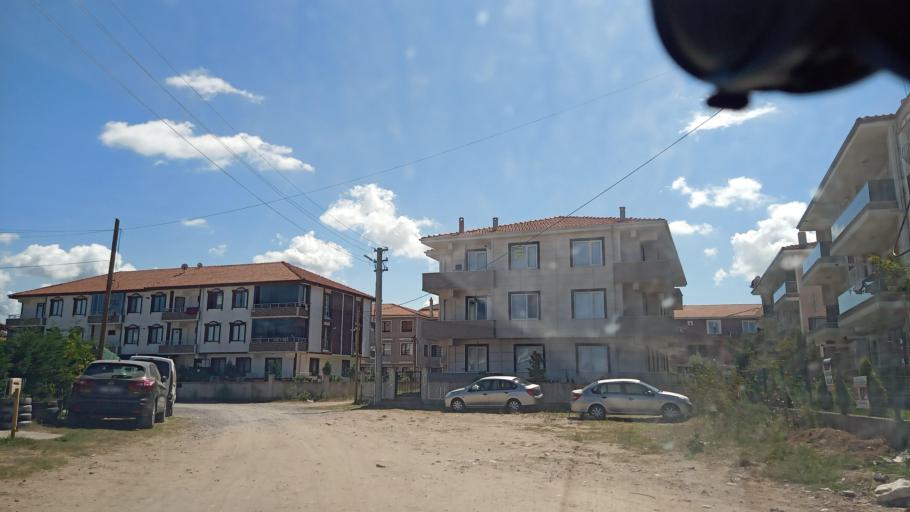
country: TR
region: Sakarya
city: Karasu
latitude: 41.1232
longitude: 30.6544
